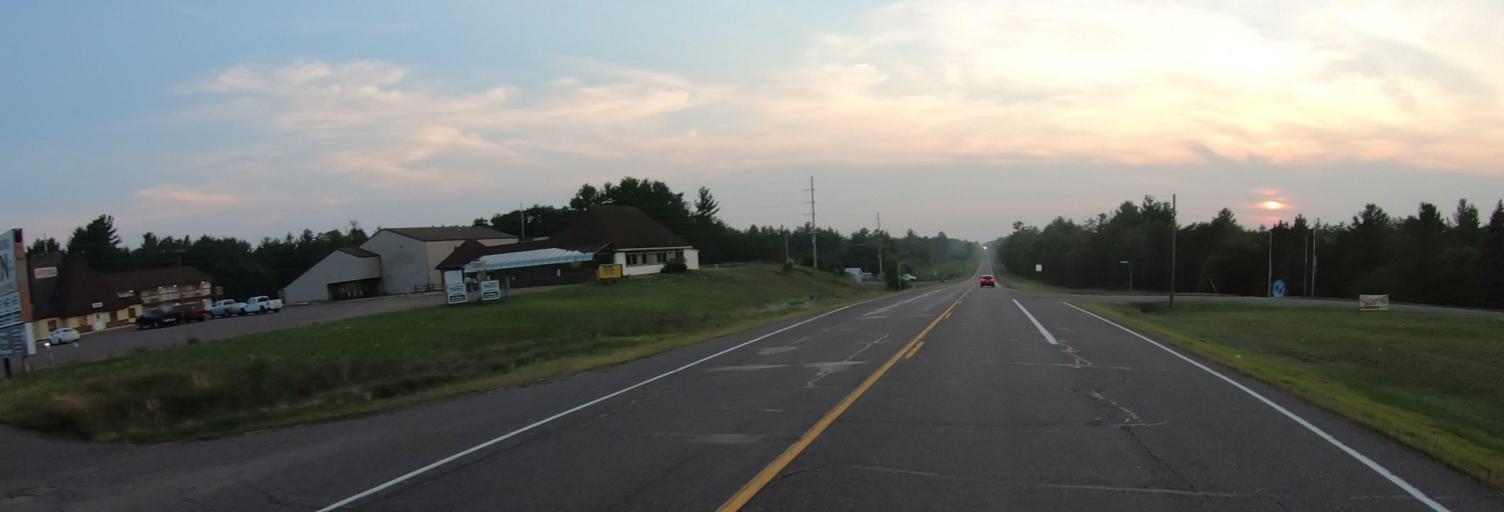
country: US
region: Wisconsin
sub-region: Burnett County
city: Grantsburg
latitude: 45.7730
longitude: -92.6988
